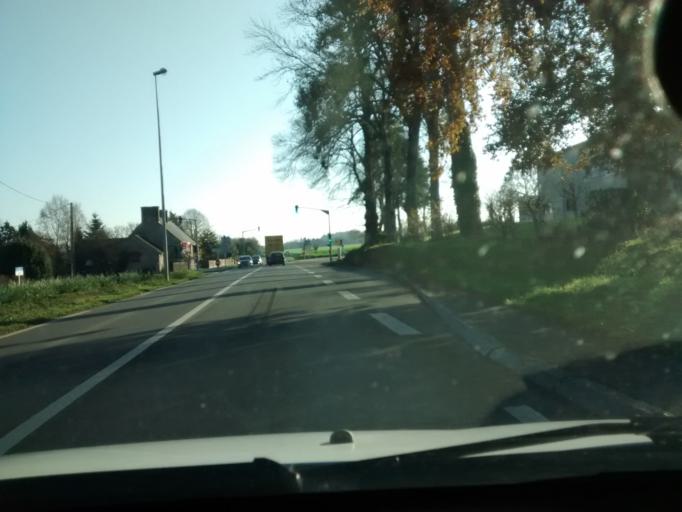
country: FR
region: Brittany
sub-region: Departement d'Ille-et-Vilaine
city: Antrain
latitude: 48.4491
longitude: -1.4753
